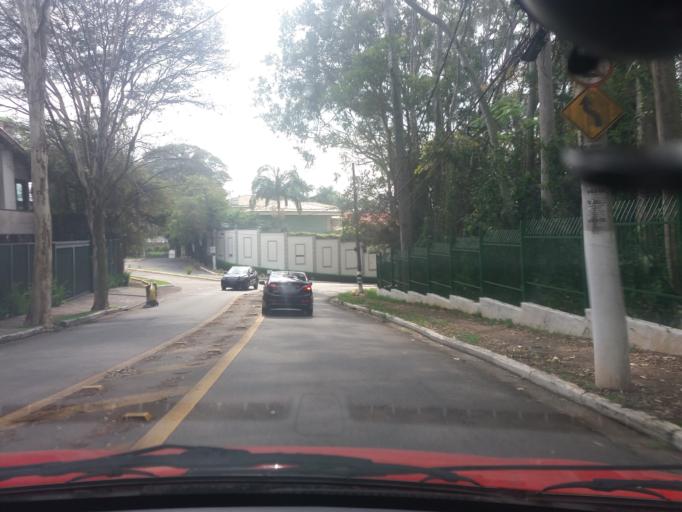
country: BR
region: Sao Paulo
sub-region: Sao Paulo
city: Sao Paulo
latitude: -23.5860
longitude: -46.7030
